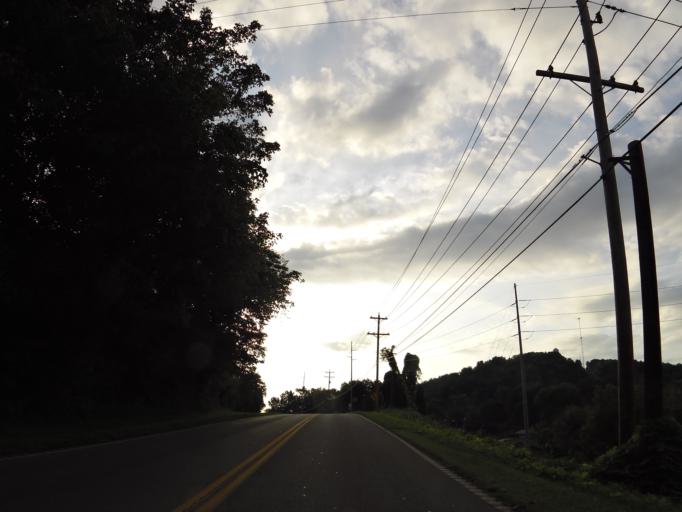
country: US
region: Tennessee
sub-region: Cocke County
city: Newport
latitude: 35.9559
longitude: -83.1617
